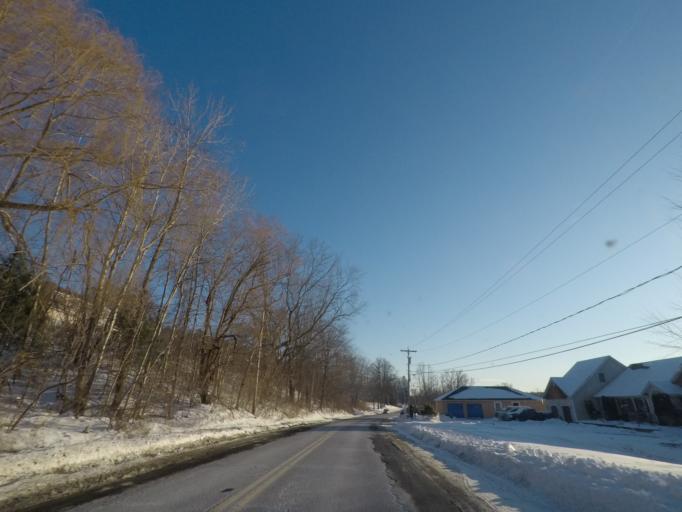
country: US
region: New York
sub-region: Saratoga County
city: Mechanicville
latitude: 42.8754
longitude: -73.6709
